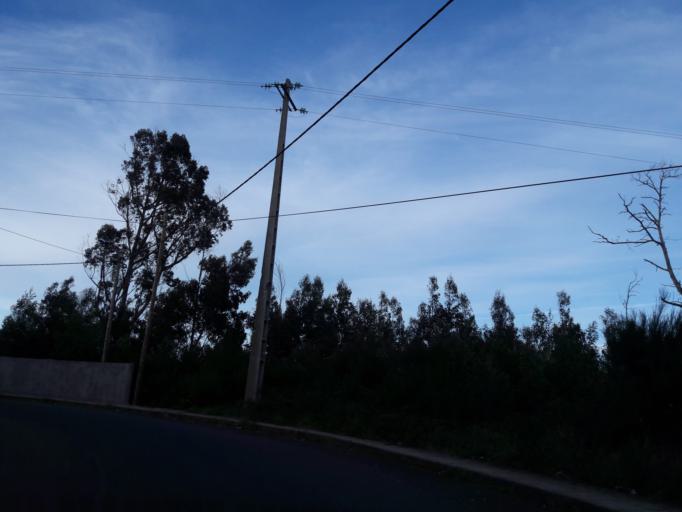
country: PT
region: Madeira
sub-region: Santa Cruz
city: Camacha
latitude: 32.6880
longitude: -16.8630
